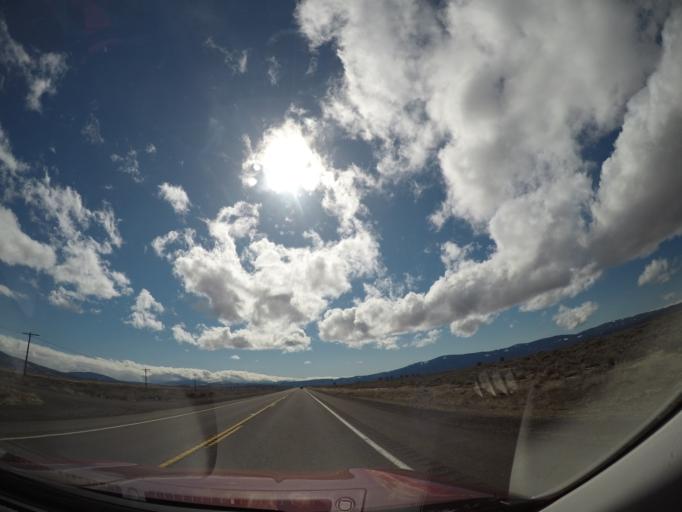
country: US
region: Oregon
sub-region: Klamath County
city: Klamath Falls
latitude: 41.9068
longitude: -121.9559
